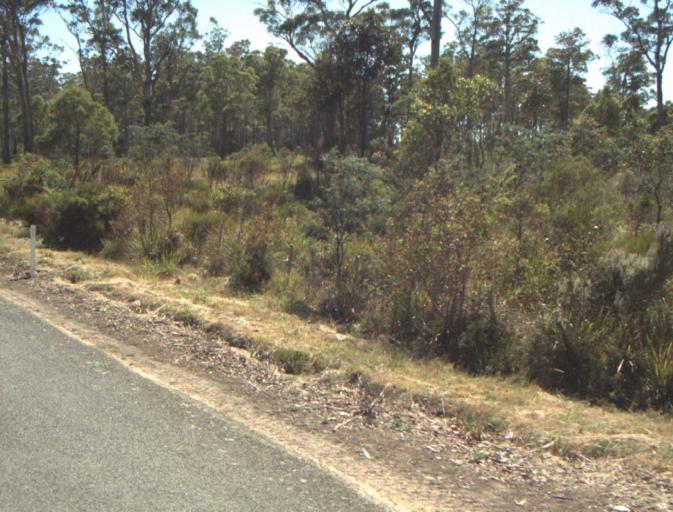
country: AU
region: Tasmania
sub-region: Launceston
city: Newstead
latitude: -41.3856
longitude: 147.2968
